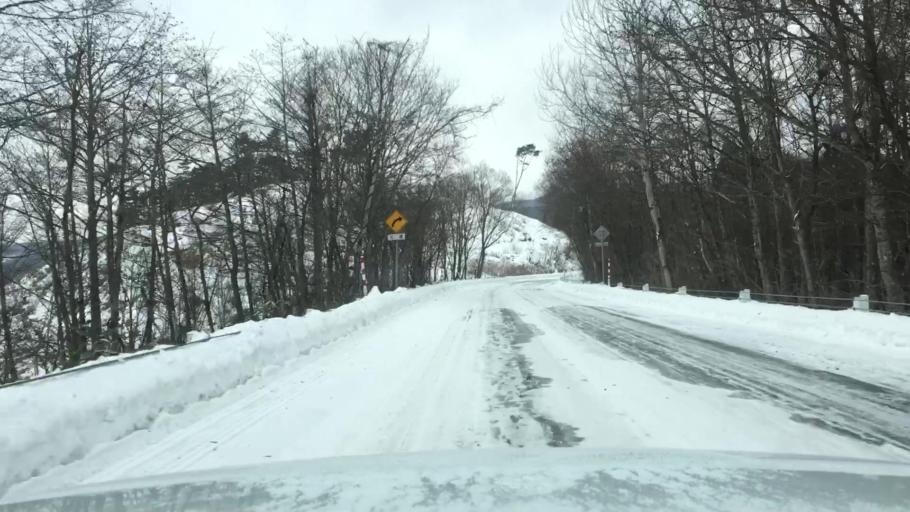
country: JP
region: Iwate
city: Shizukuishi
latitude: 39.9390
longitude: 140.9990
